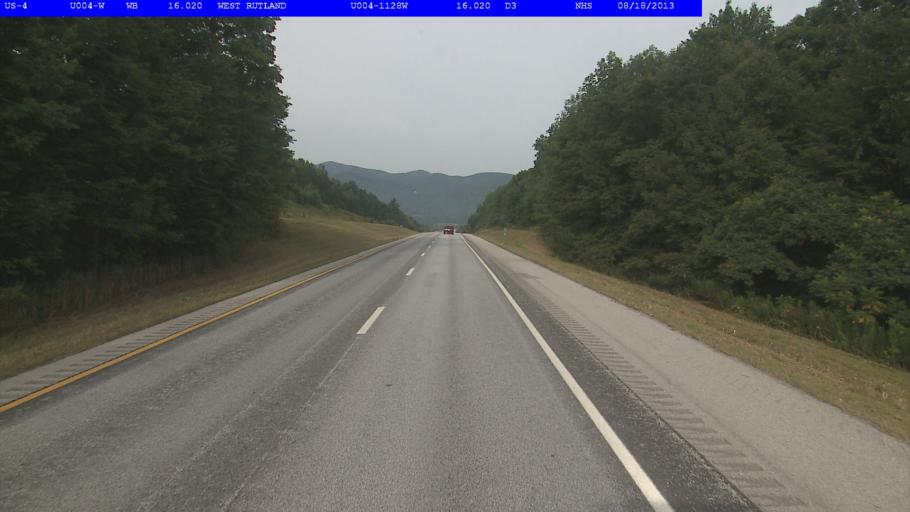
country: US
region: Vermont
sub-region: Rutland County
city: West Rutland
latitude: 43.5931
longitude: -73.0170
